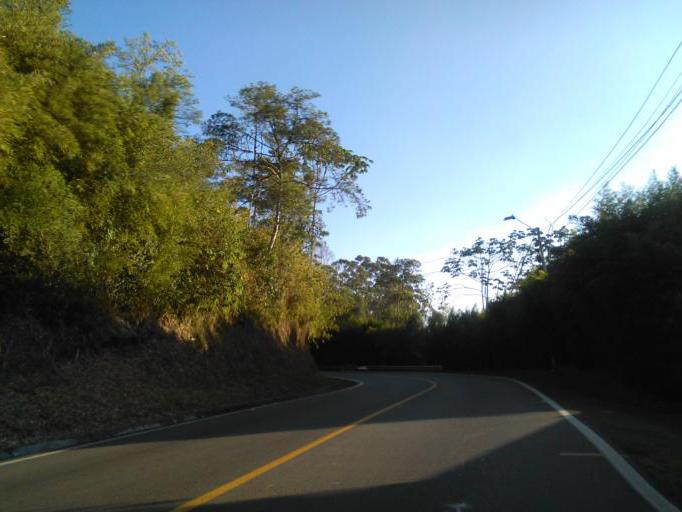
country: CO
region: Antioquia
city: La Ceja
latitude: 6.0104
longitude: -75.4073
